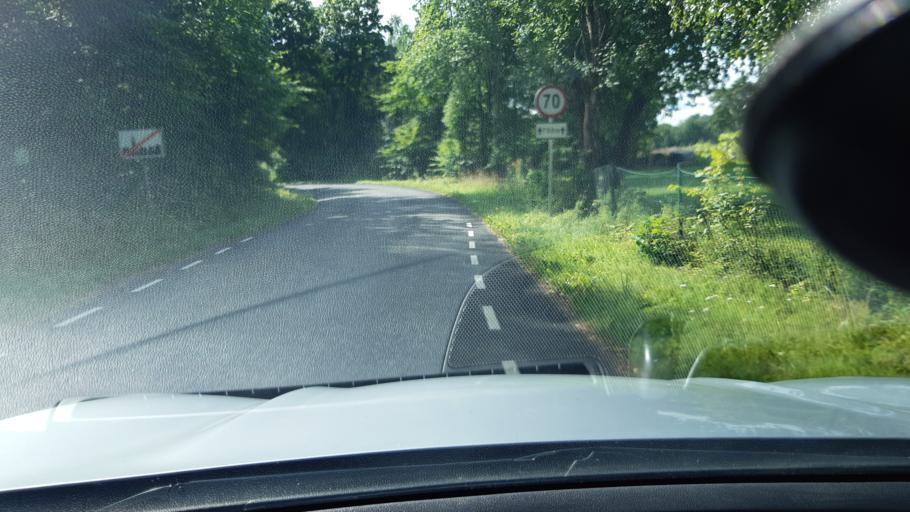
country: EE
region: Raplamaa
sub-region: Kehtna vald
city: Kehtna
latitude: 58.9390
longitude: 24.8972
